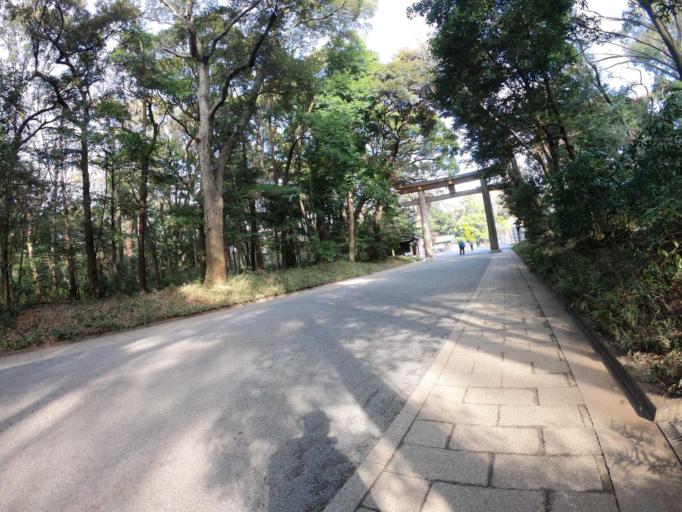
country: JP
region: Chiba
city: Ichihara
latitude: 35.4593
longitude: 140.0192
